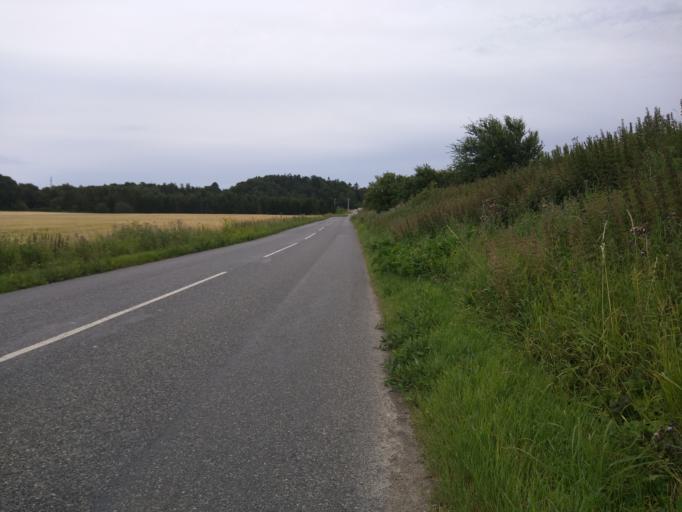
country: DK
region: Zealand
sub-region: Kalundborg Kommune
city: Svebolle
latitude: 55.6714
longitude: 11.3425
